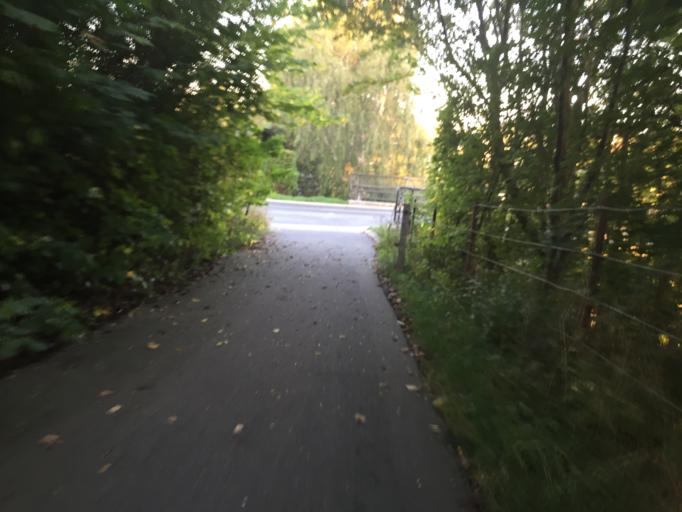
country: DK
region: Capital Region
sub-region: Egedal Kommune
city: Smorumnedre
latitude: 55.7504
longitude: 12.3089
